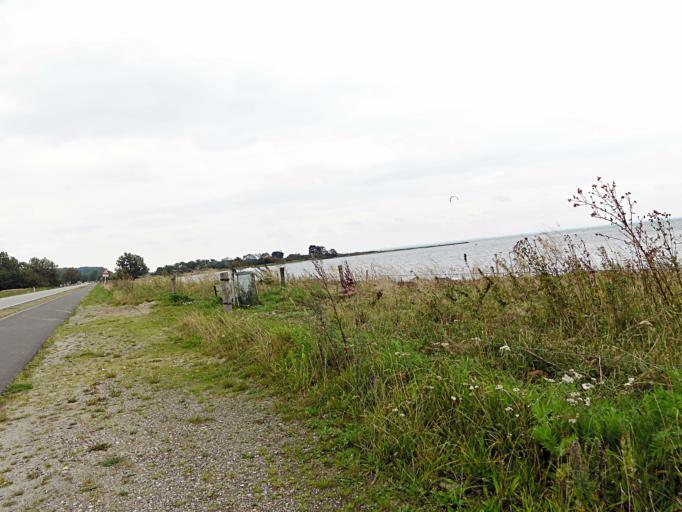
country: DK
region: Capital Region
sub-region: Fredensborg Kommune
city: Niva
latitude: 55.9330
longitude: 12.5215
